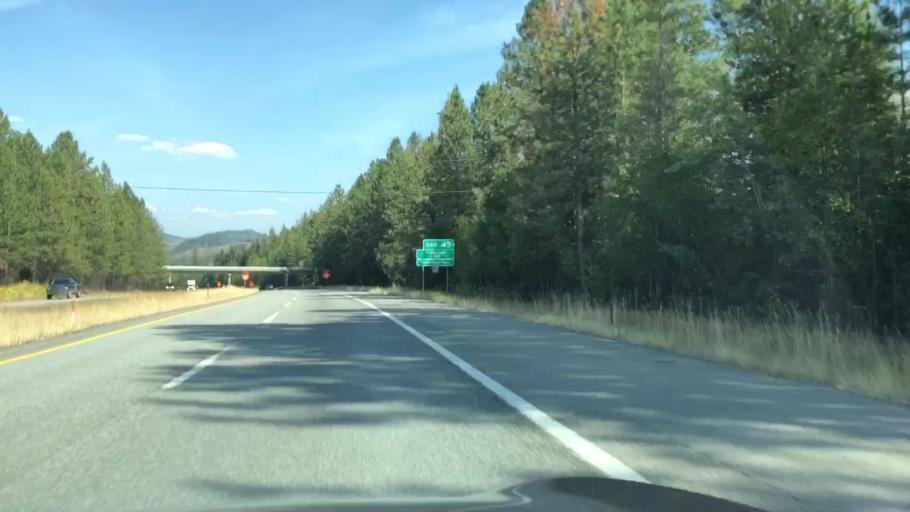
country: US
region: Idaho
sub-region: Shoshone County
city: Pinehurst
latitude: 47.5504
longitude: -116.2985
